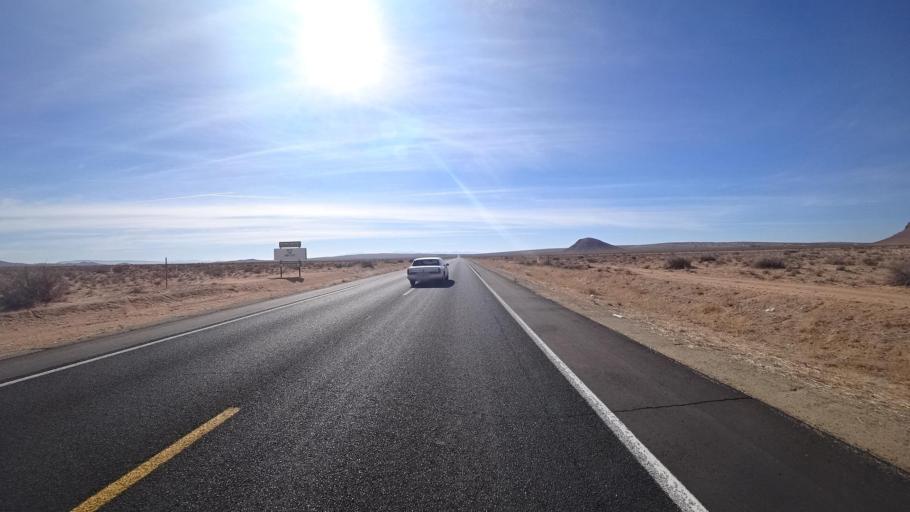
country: US
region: California
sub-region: Kern County
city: California City
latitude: 35.0952
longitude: -117.9175
